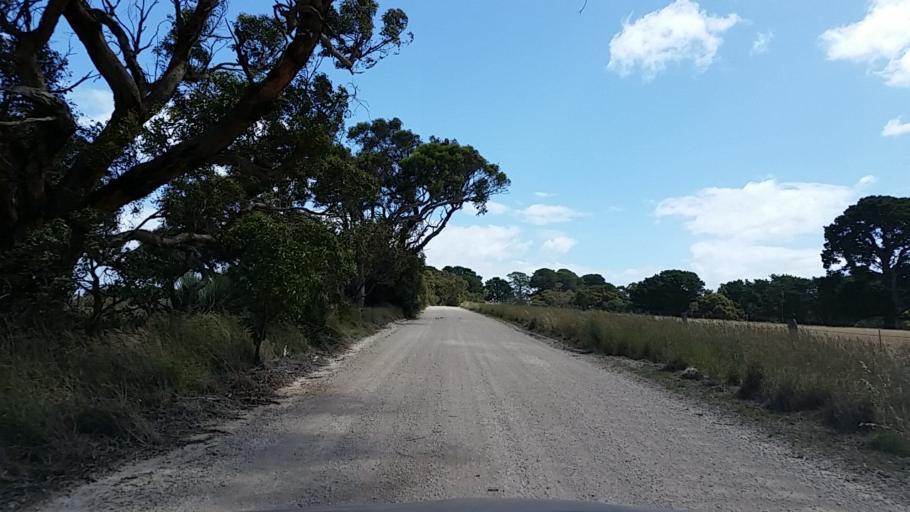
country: AU
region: South Australia
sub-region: Alexandrina
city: Port Elliot
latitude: -35.4519
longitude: 138.6463
